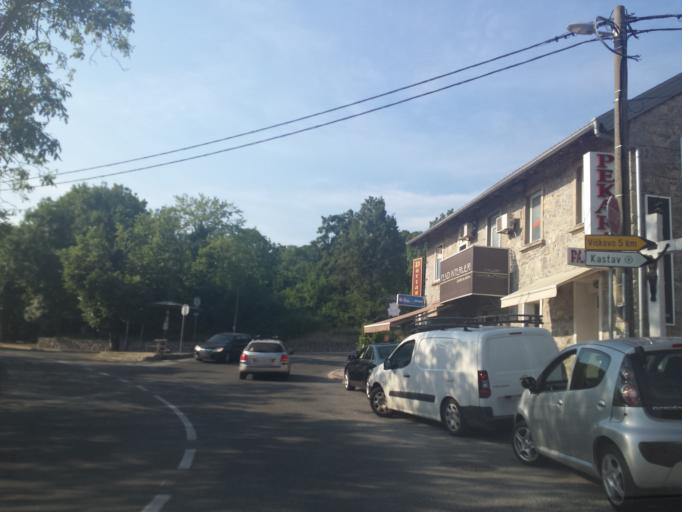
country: HR
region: Primorsko-Goranska
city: Kastav
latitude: 45.3721
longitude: 14.3451
